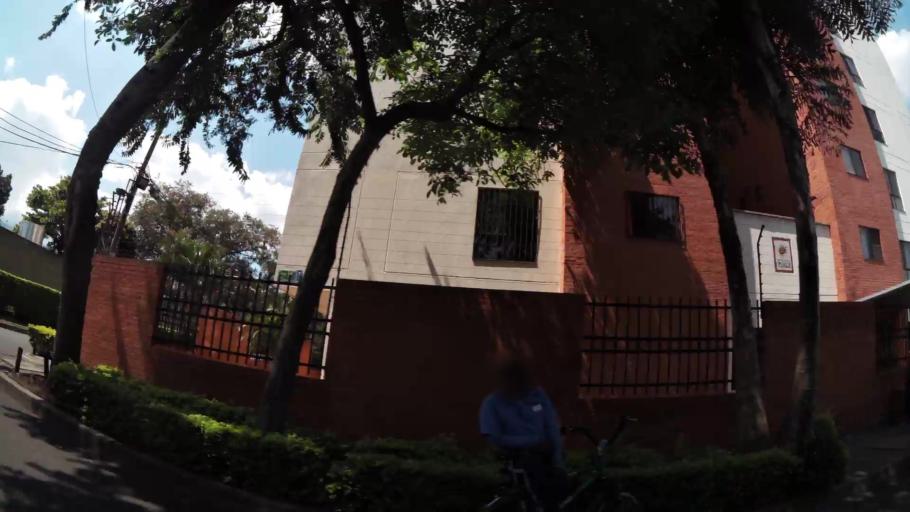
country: CO
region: Valle del Cauca
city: Cali
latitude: 3.4106
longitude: -76.5469
